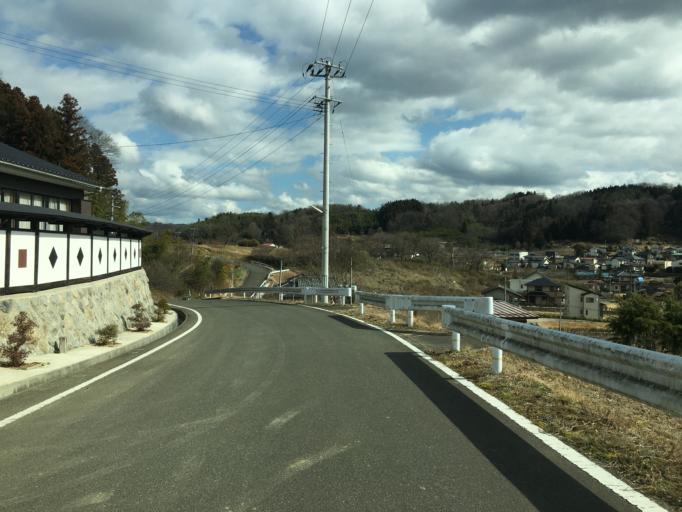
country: JP
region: Fukushima
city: Fukushima-shi
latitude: 37.6598
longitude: 140.5398
